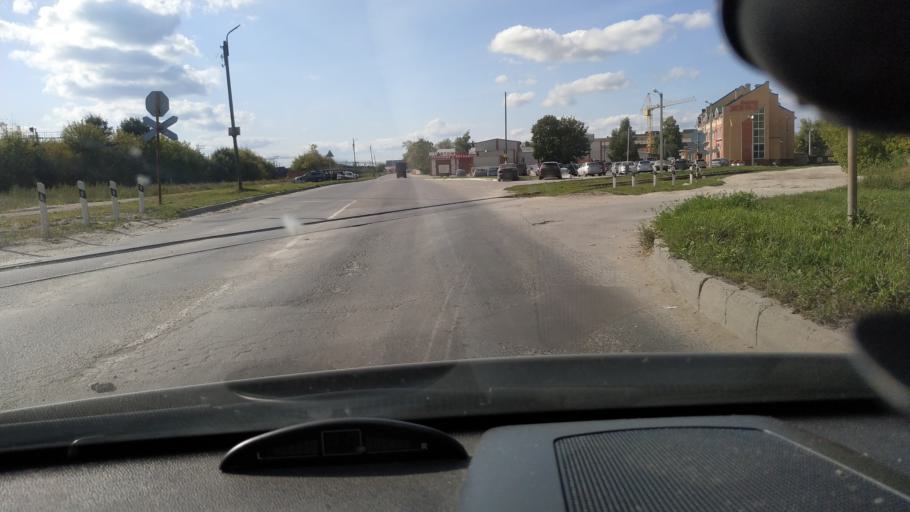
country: RU
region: Rjazan
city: Ryazan'
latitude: 54.6517
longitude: 39.6466
